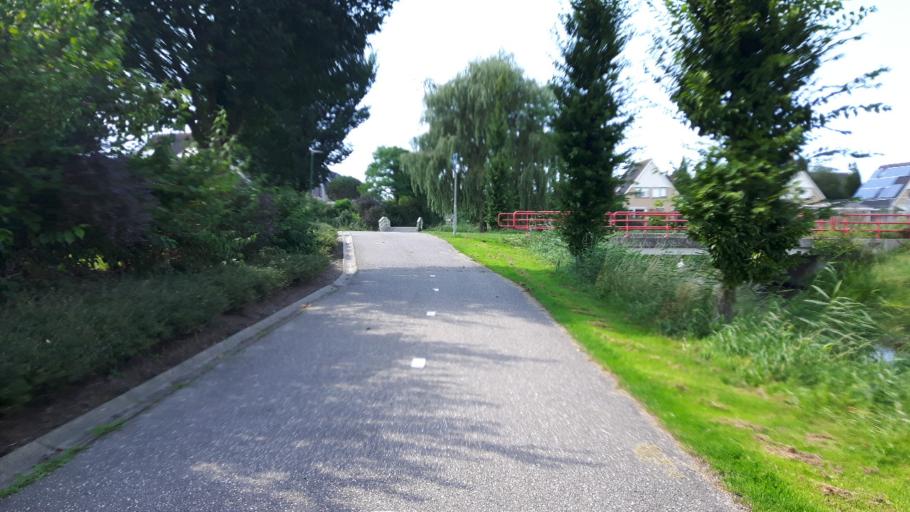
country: NL
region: North Holland
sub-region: Gemeente Medemblik
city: Opperdoes
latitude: 52.7184
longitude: 5.0804
